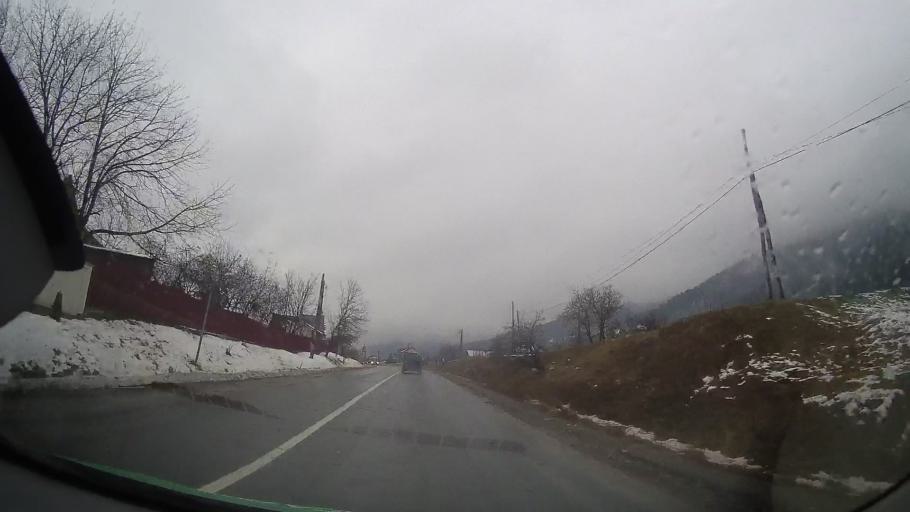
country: RO
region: Neamt
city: Viisoara
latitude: 46.9313
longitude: 26.2151
